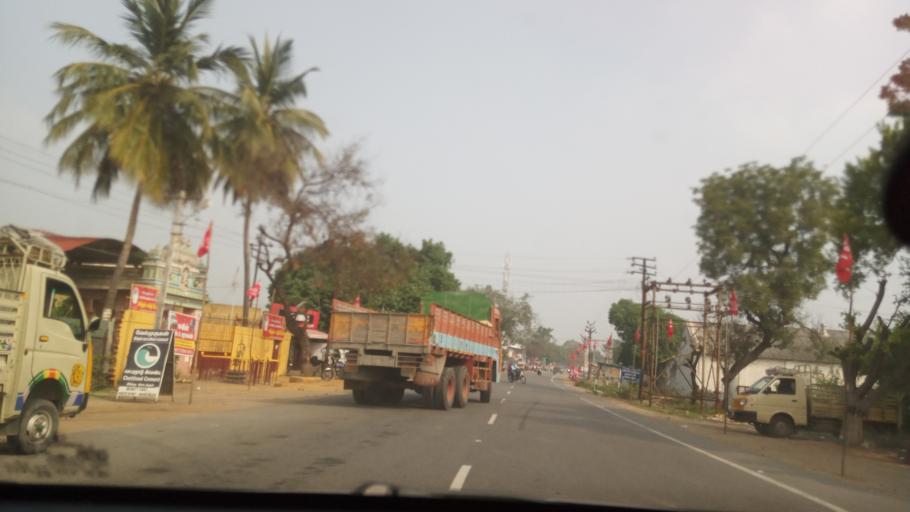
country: IN
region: Tamil Nadu
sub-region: Erode
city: Punjai Puliyampatti
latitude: 11.3563
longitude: 77.1695
